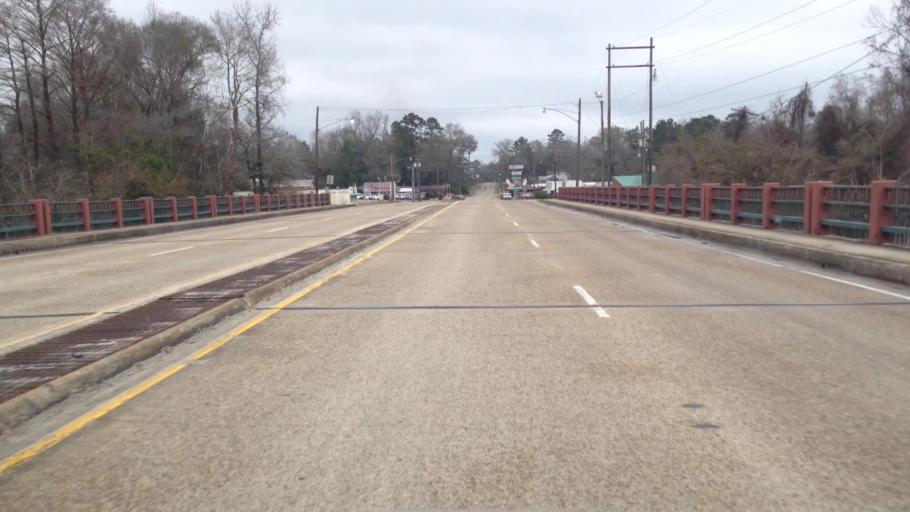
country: US
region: Louisiana
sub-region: Washington Parish
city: Bogalusa
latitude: 30.7822
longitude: -89.8554
